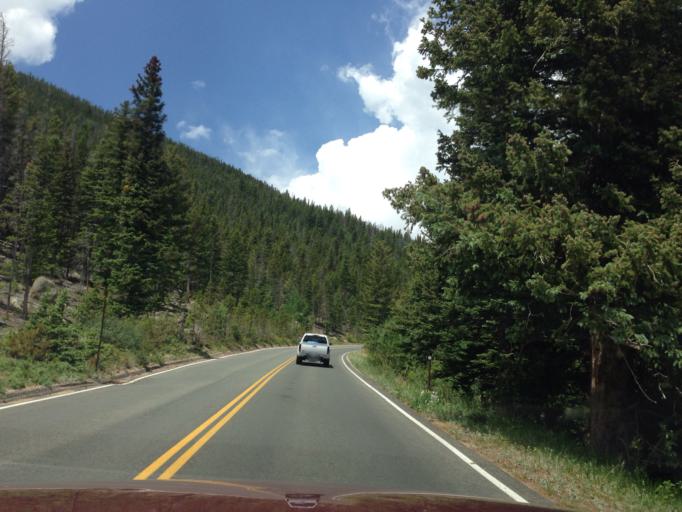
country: US
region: Colorado
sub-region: Larimer County
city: Estes Park
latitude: 40.3966
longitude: -105.6356
